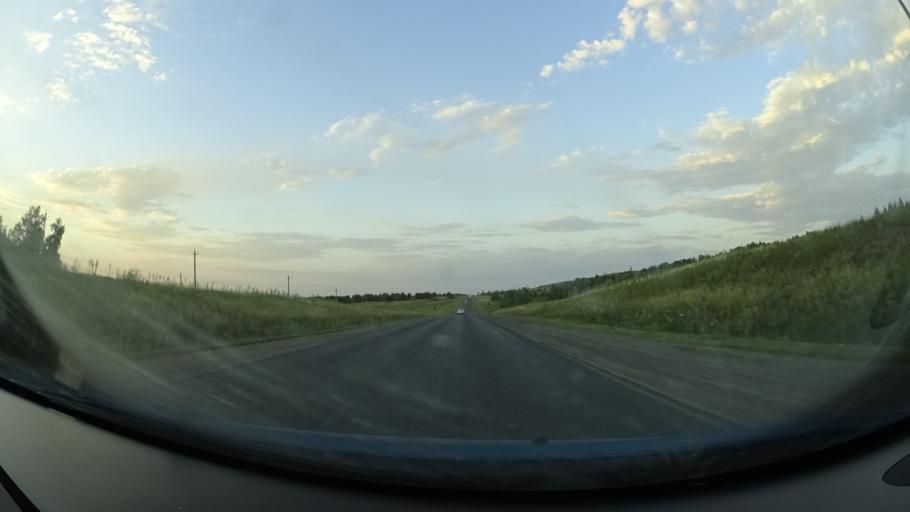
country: RU
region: Orenburg
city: Severnoye
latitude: 54.1807
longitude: 52.6588
